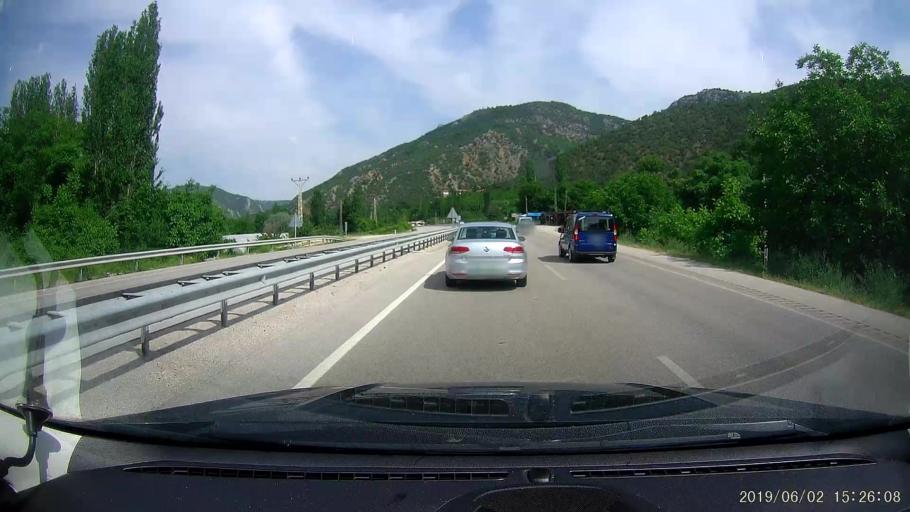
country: TR
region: Amasya
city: Saraycik
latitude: 40.9879
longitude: 35.0310
